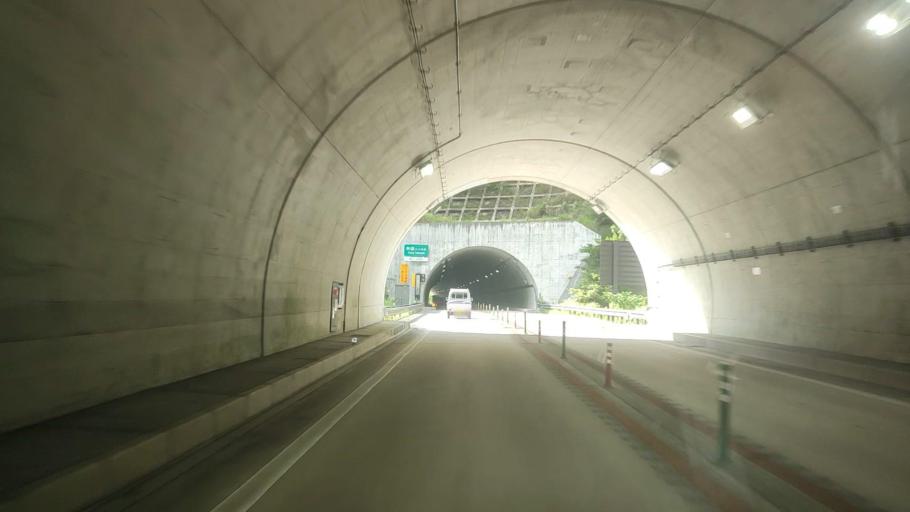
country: JP
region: Wakayama
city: Tanabe
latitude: 33.5835
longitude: 135.4507
